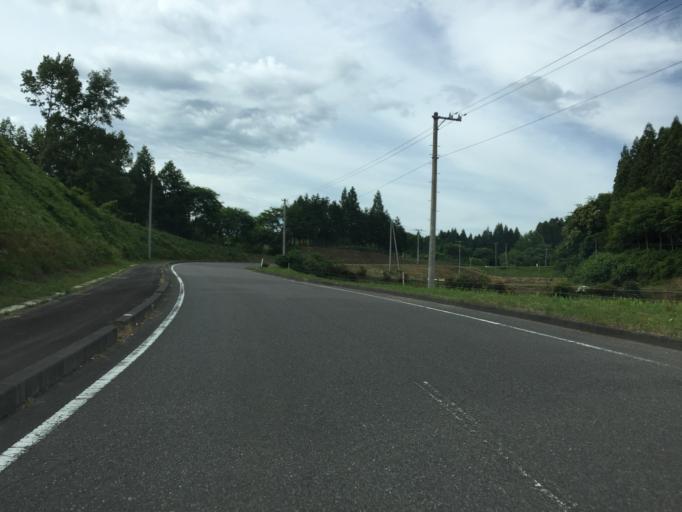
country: JP
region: Fukushima
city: Funehikimachi-funehiki
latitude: 37.5070
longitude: 140.5600
